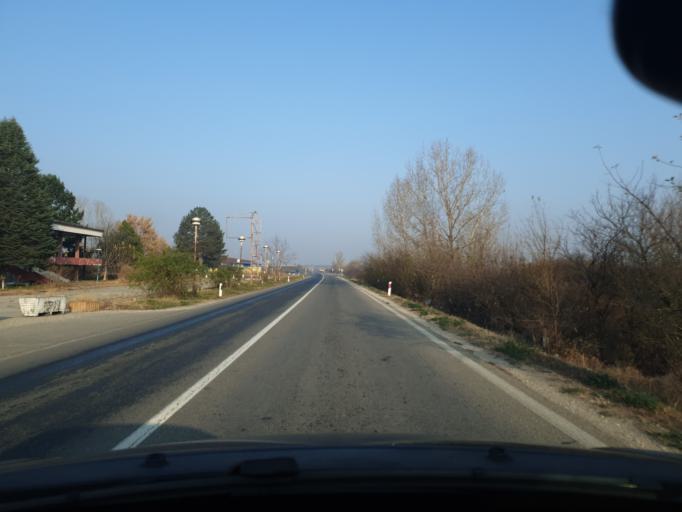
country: RS
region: Central Serbia
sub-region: Jablanicki Okrug
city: Leskovac
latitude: 43.0023
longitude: 21.9669
